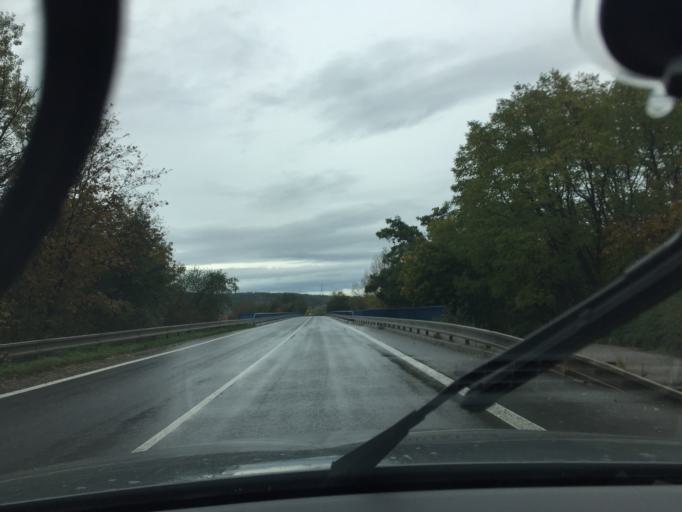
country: CZ
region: Central Bohemia
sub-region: Okres Melnik
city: Veltrusy
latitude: 50.2784
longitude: 14.3174
